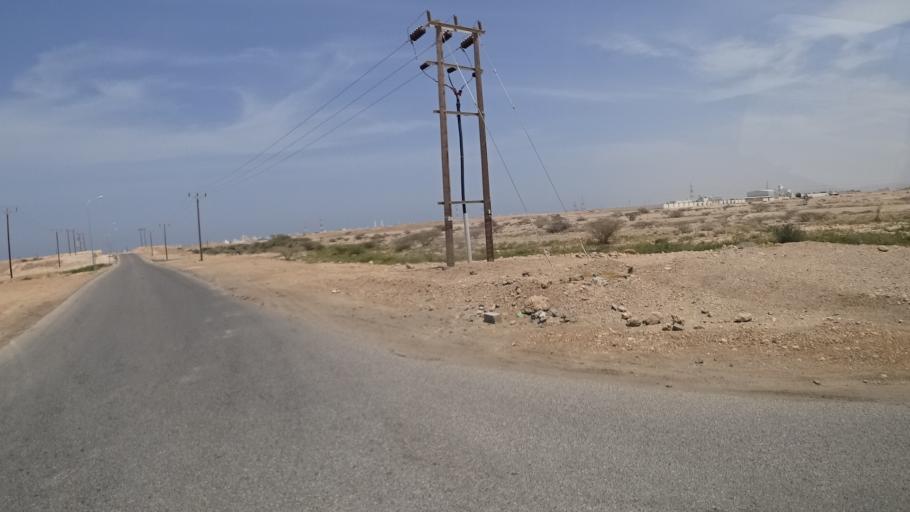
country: OM
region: Ash Sharqiyah
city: Sur
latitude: 22.6097
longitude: 59.4491
